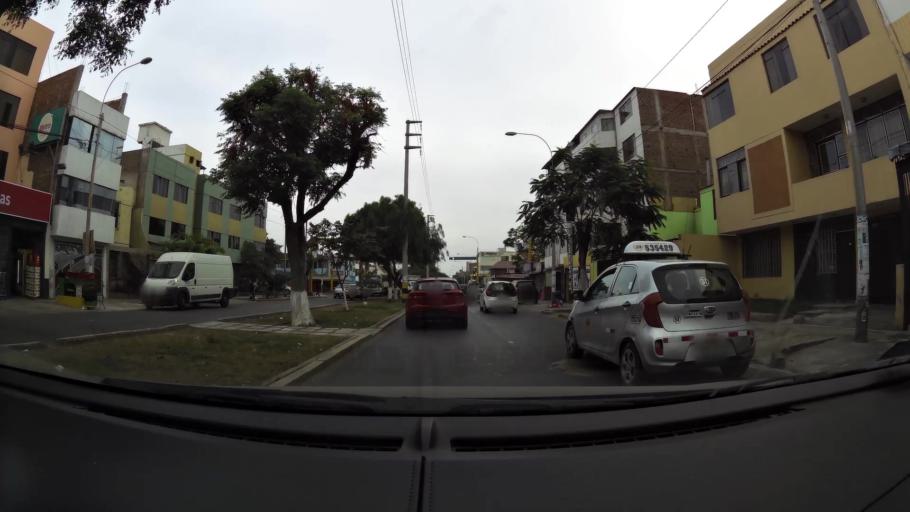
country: PE
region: La Libertad
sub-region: Provincia de Trujillo
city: Trujillo
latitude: -8.0997
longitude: -79.0313
